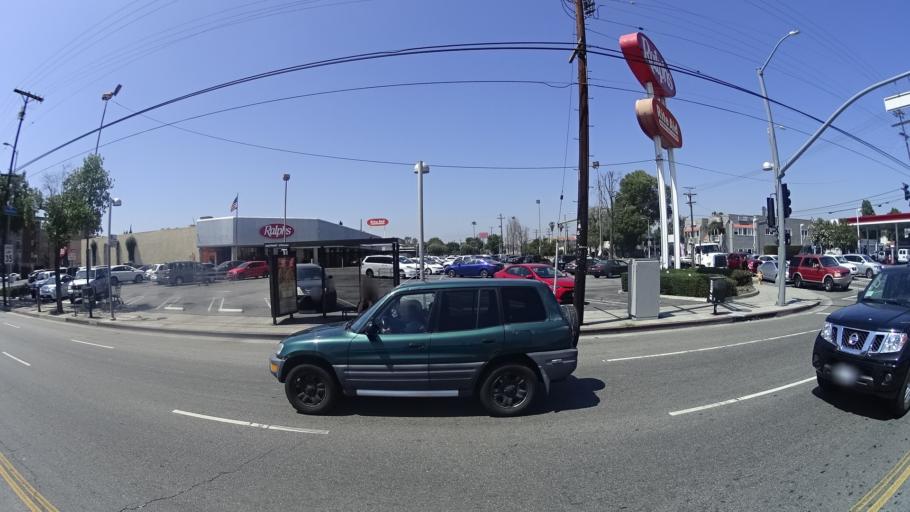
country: US
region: California
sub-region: Los Angeles County
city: Van Nuys
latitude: 34.2012
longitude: -118.4316
